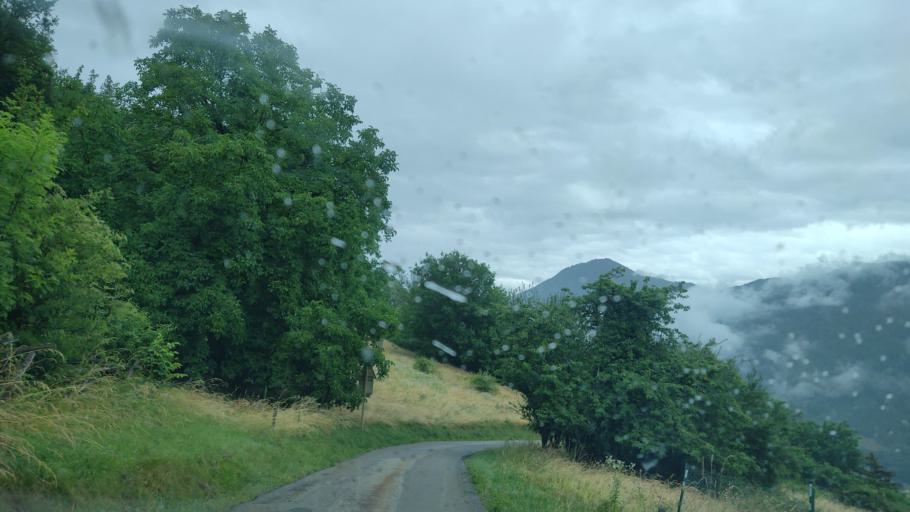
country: FR
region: Rhone-Alpes
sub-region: Departement de la Savoie
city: Coise-Saint-Jean-Pied-Gauthier
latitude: 45.5102
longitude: 6.1518
